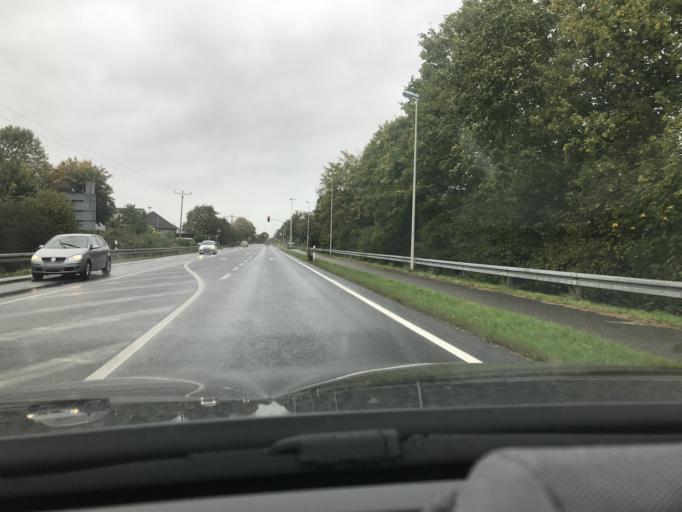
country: DE
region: North Rhine-Westphalia
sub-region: Regierungsbezirk Dusseldorf
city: Nettetal
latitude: 51.3291
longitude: 6.2786
